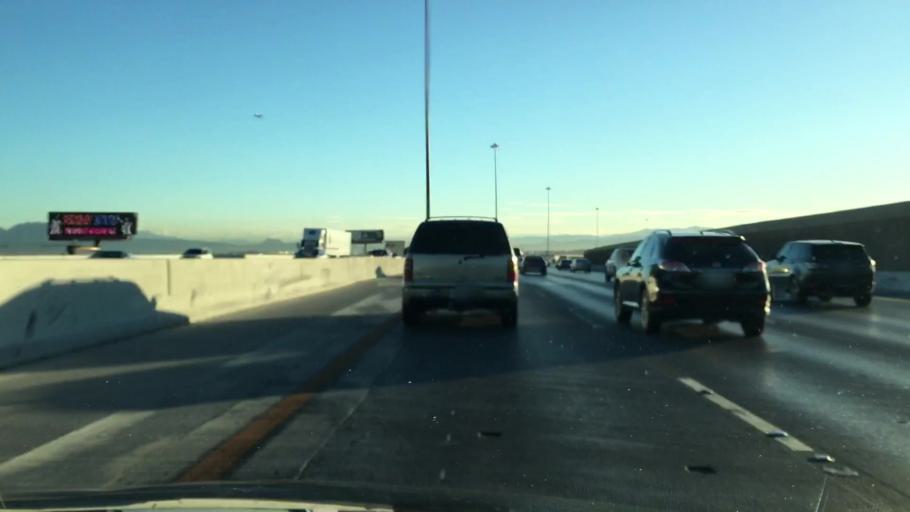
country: US
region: Nevada
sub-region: Clark County
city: Spring Valley
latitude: 36.0684
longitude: -115.2031
